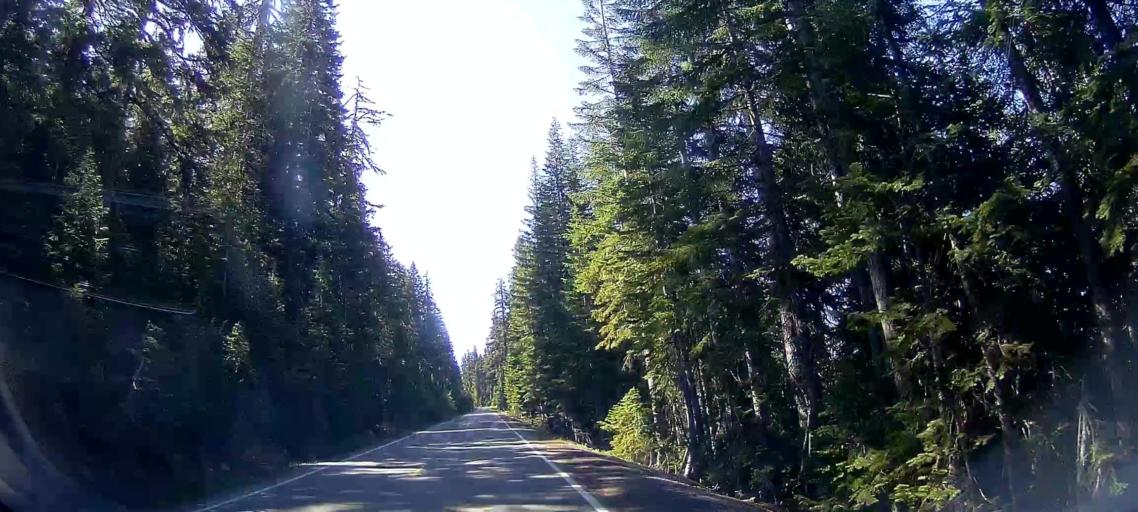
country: US
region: Oregon
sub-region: Jackson County
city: Shady Cove
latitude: 42.8854
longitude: -122.1301
